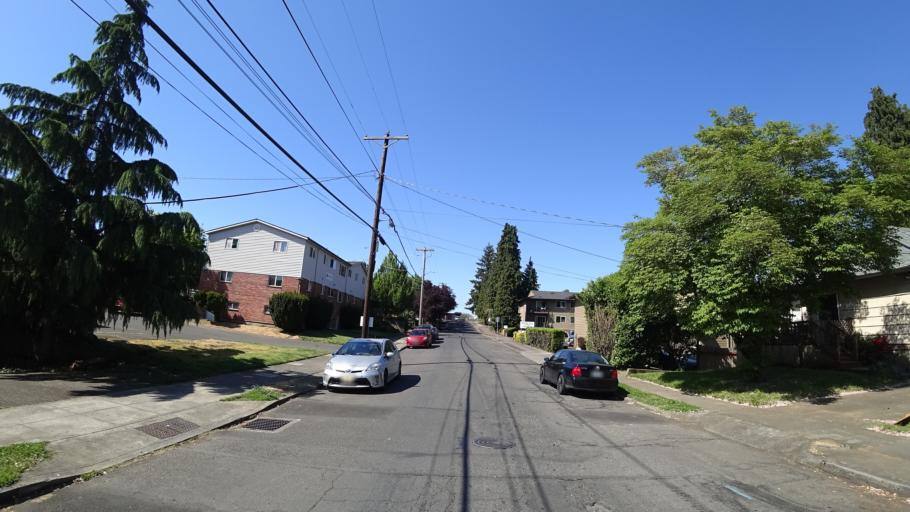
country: US
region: Oregon
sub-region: Clackamas County
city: Milwaukie
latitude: 45.4962
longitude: -122.6208
